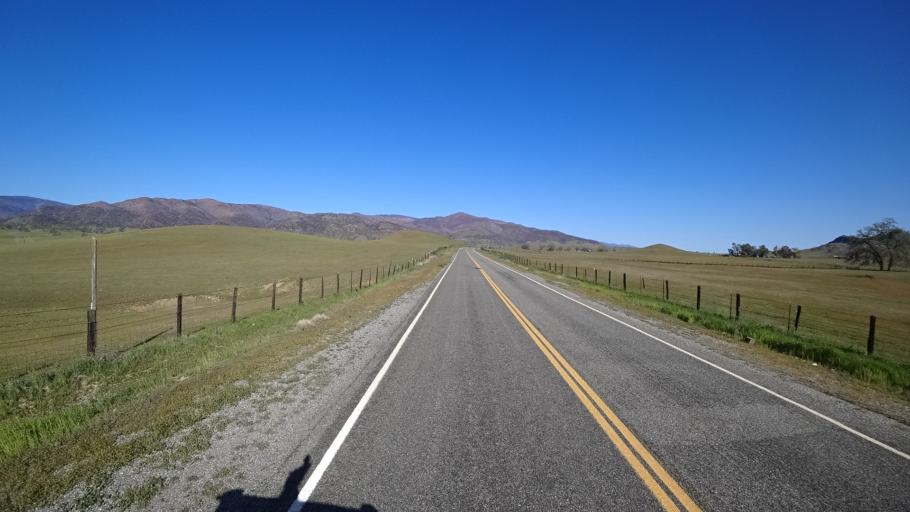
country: US
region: California
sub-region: Glenn County
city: Orland
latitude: 39.6884
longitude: -122.5435
